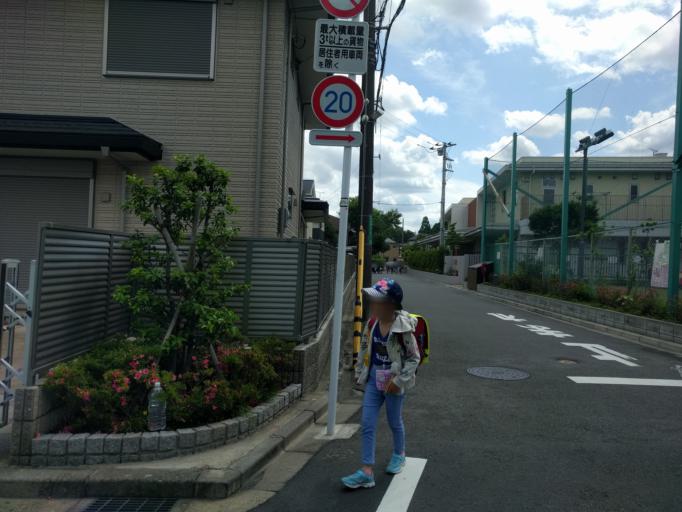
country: JP
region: Tokyo
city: Chofugaoka
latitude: 35.6370
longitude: 139.5709
